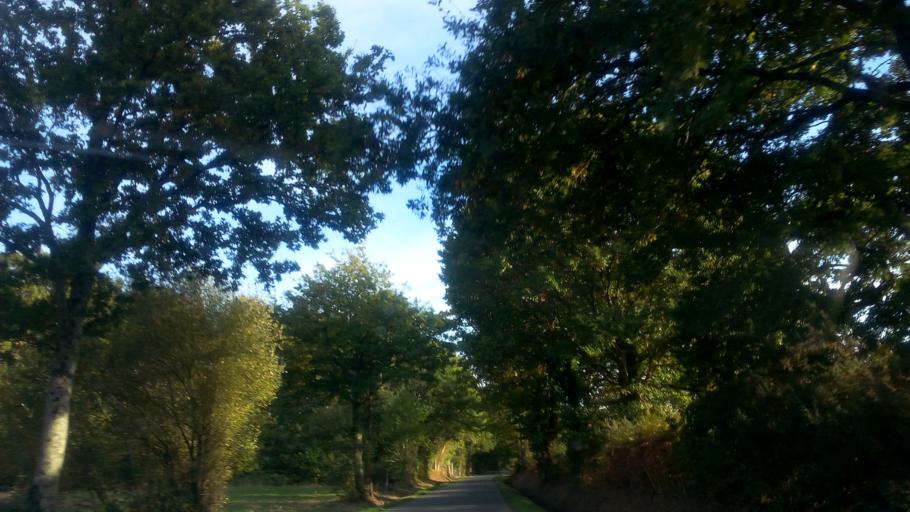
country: FR
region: Brittany
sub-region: Departement du Morbihan
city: Saint-Perreux
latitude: 47.6889
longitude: -2.1025
